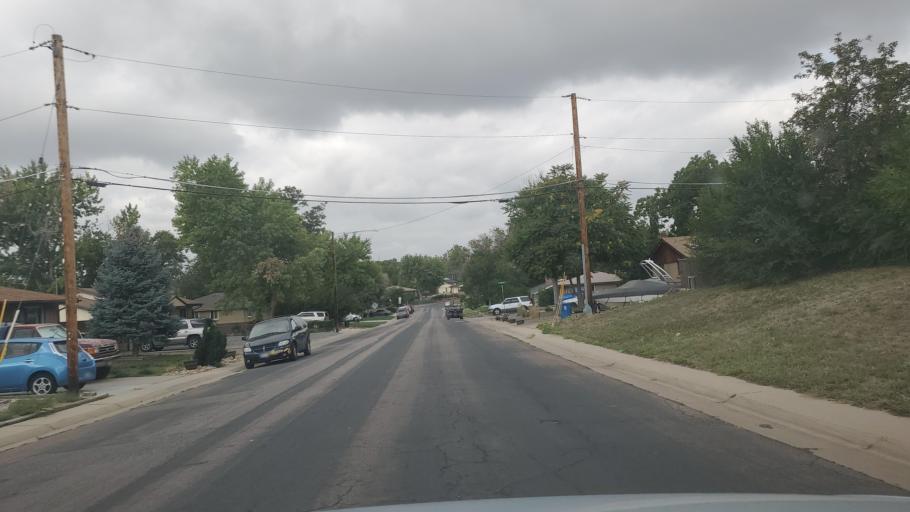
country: US
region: Colorado
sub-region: Adams County
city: Welby
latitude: 39.8493
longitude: -104.9686
